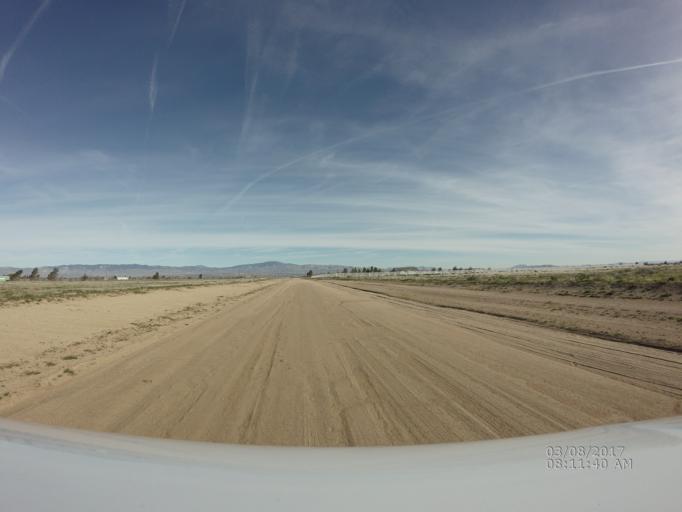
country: US
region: California
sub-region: Los Angeles County
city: Green Valley
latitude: 34.7504
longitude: -118.4487
